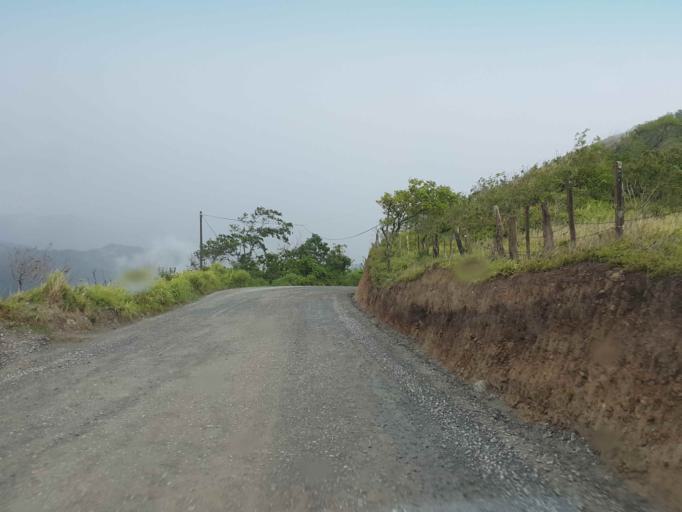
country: CR
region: Guanacaste
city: Juntas
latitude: 10.2547
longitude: -84.8400
